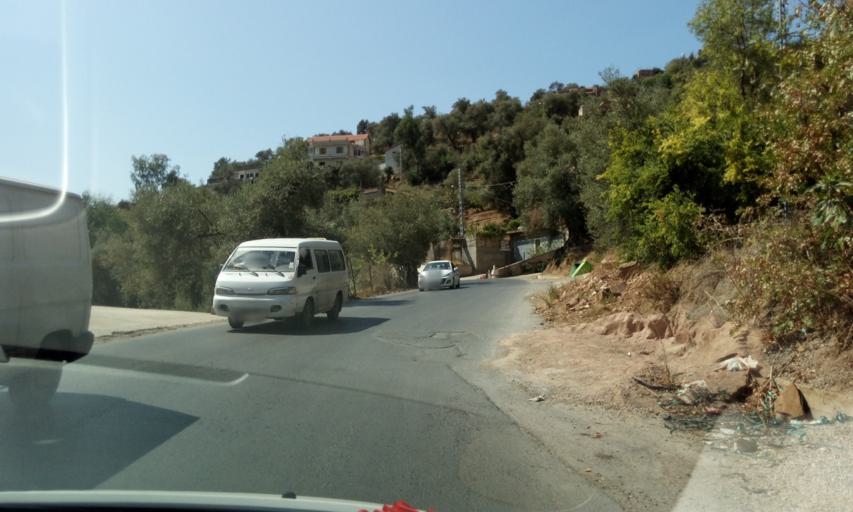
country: DZ
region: Tizi Ouzou
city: Chemini
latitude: 36.6195
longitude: 4.6628
